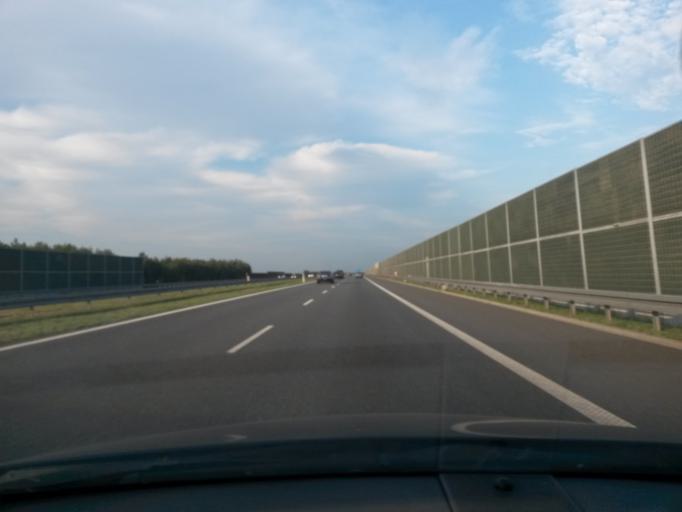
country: PL
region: Lodz Voivodeship
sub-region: powiat Lowicki
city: Bobrowniki
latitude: 52.0347
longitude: 20.0184
